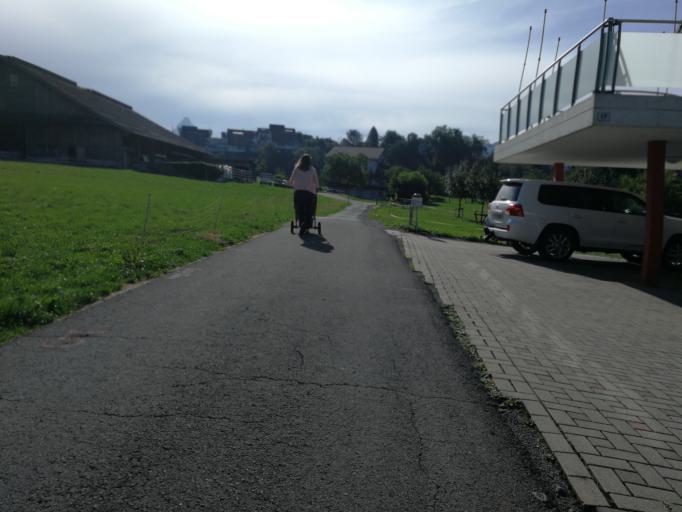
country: CH
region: Schwyz
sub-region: Bezirk Schwyz
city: Goldau
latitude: 47.0547
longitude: 8.5432
